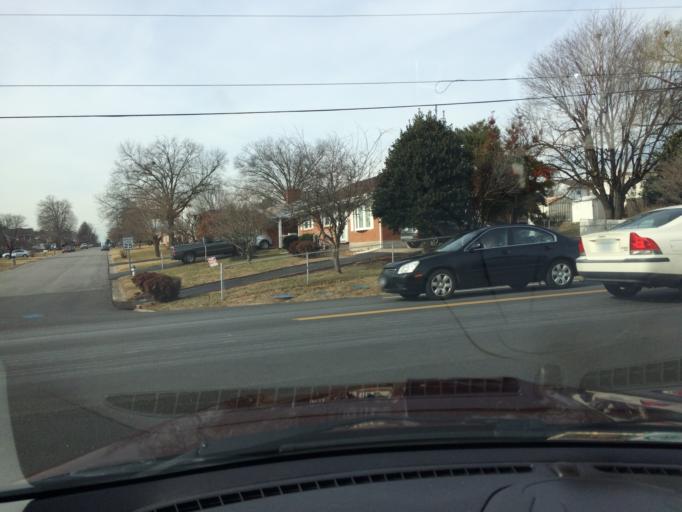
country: US
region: Virginia
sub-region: Roanoke County
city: Hollins
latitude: 37.3302
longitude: -79.9371
